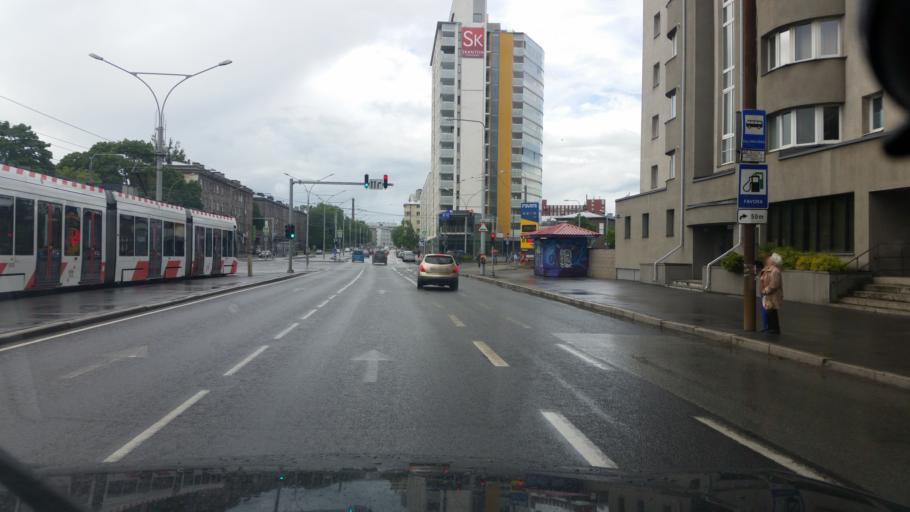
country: EE
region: Harju
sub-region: Tallinna linn
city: Tallinn
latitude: 59.4155
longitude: 24.7396
